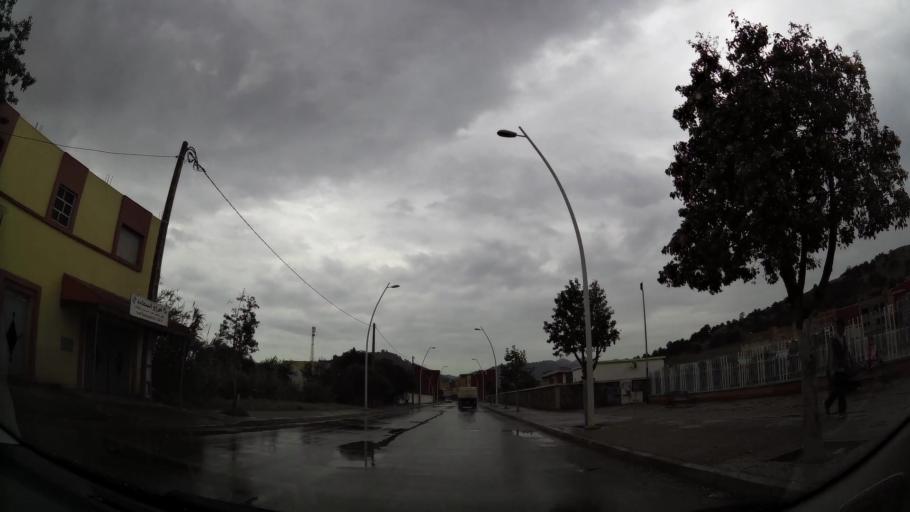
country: MA
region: Oriental
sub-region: Nador
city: Nador
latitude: 35.1481
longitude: -2.9788
